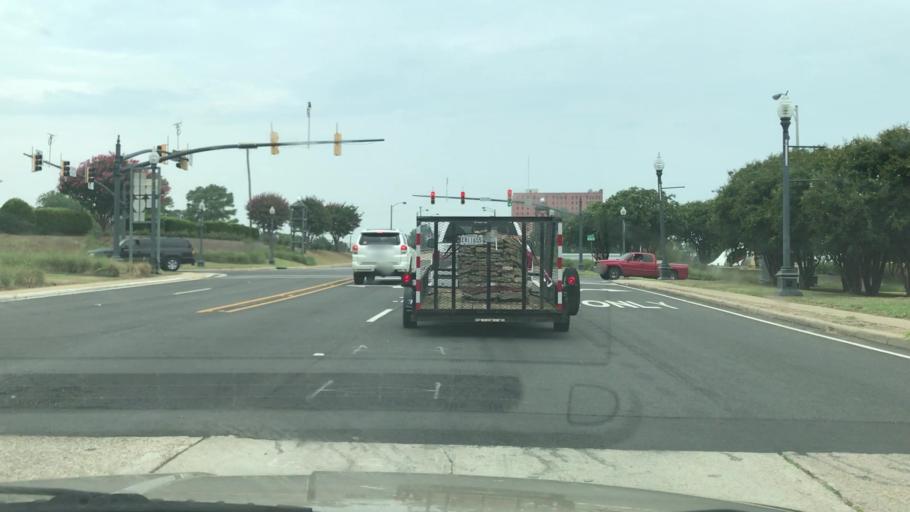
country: US
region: Louisiana
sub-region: Bossier Parish
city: Bossier City
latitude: 32.5050
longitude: -93.7469
